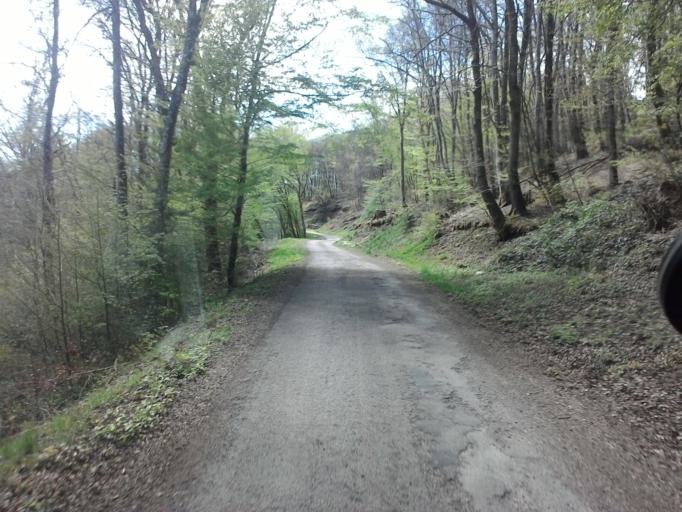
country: FR
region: Bourgogne
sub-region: Departement de la Nievre
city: Lormes
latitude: 47.3056
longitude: 3.9148
